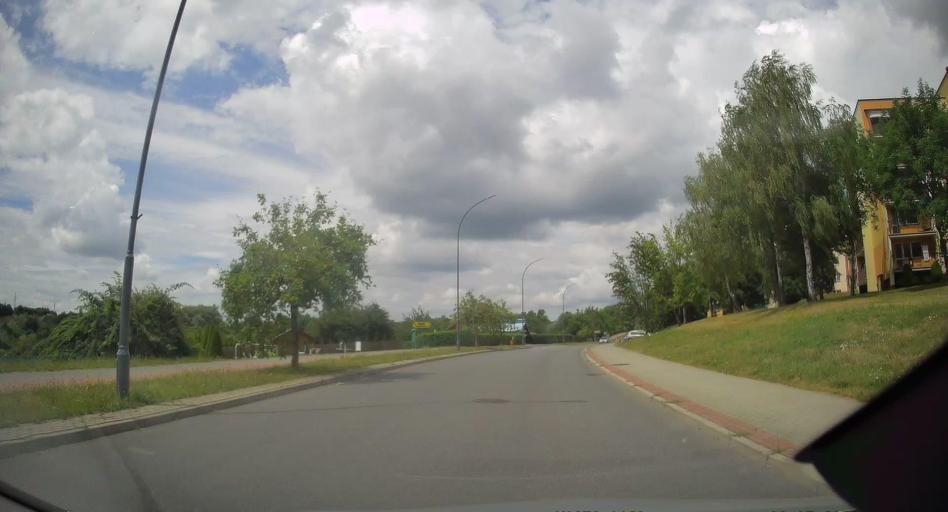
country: PL
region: Subcarpathian Voivodeship
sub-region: Powiat ropczycko-sedziszowski
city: Ropczyce
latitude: 50.0572
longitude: 21.6000
